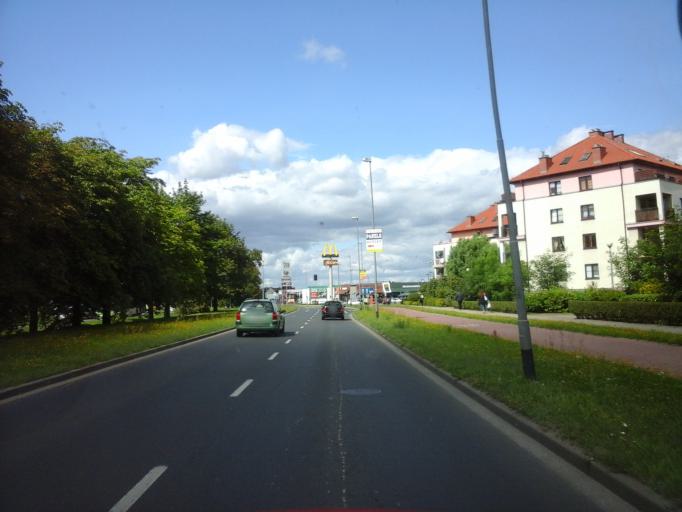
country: PL
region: West Pomeranian Voivodeship
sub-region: Powiat policki
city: Przeclaw
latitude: 53.4253
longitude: 14.4891
